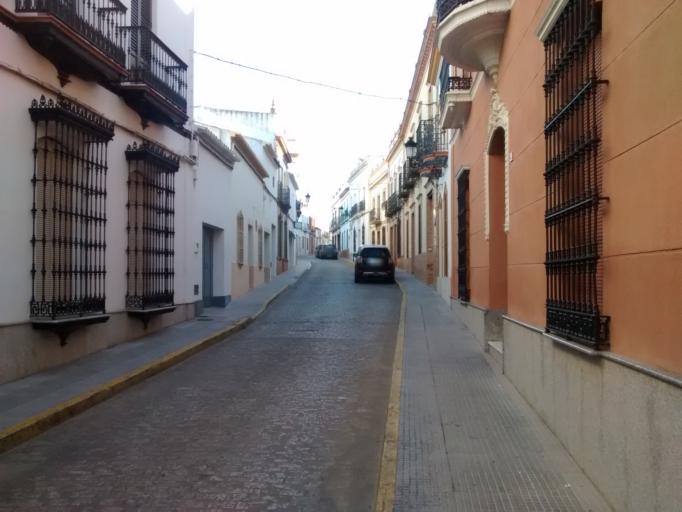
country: ES
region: Andalusia
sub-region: Provincia de Huelva
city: Bollullos par del Condado
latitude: 37.3076
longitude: -6.5968
